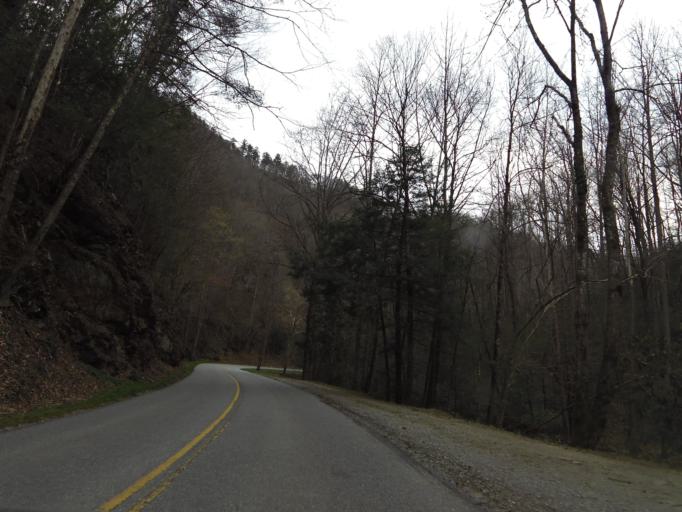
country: US
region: Tennessee
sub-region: Sevier County
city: Pigeon Forge
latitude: 35.6524
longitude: -83.7095
